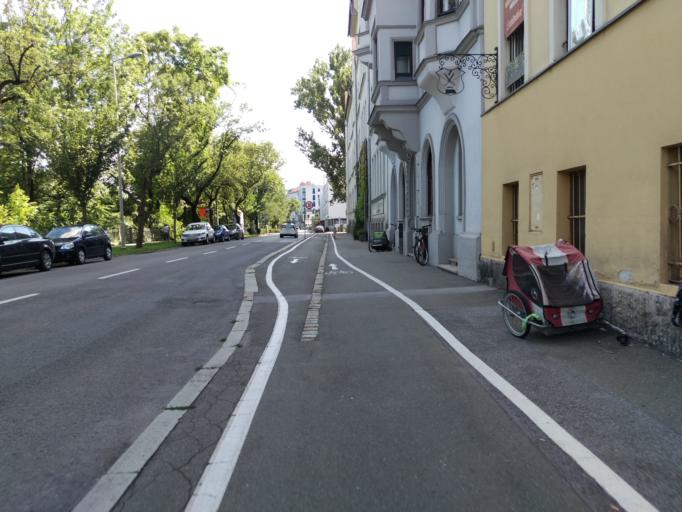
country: AT
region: Styria
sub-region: Graz Stadt
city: Graz
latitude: 47.0639
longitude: 15.4338
